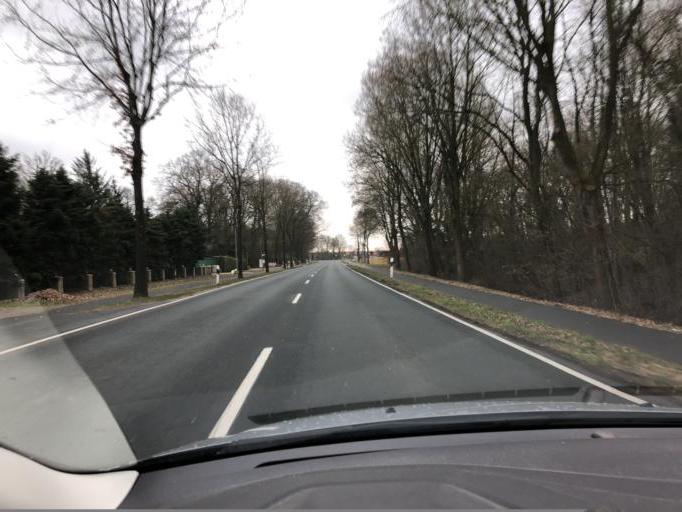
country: DE
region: Lower Saxony
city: Wiefelstede
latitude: 53.1747
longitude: 8.1311
